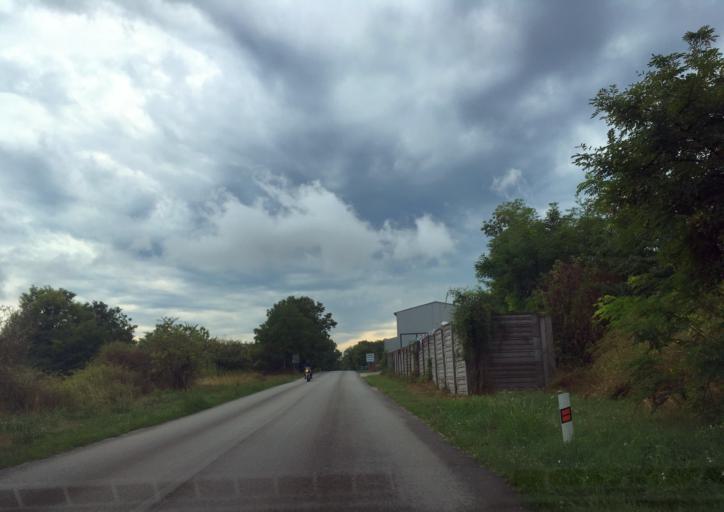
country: SK
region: Nitriansky
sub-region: Okres Nove Zamky
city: Sturovo
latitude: 47.8034
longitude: 18.6887
